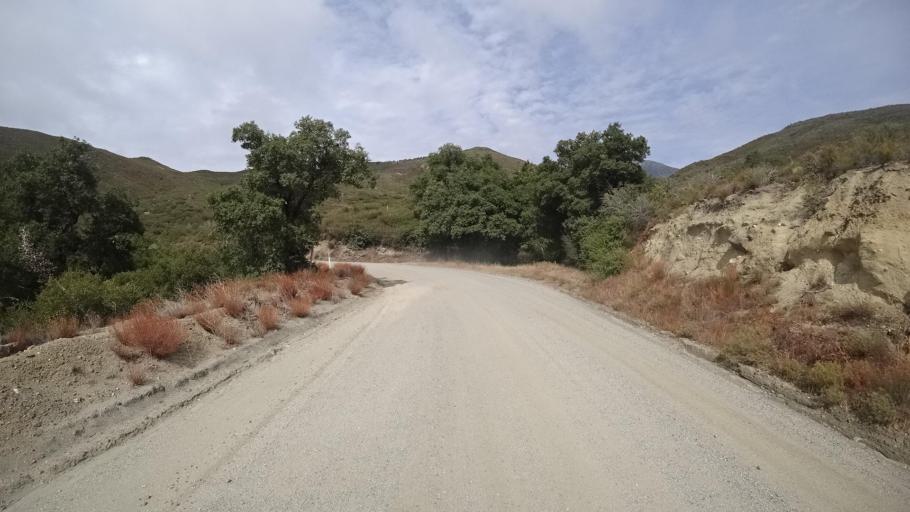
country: US
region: California
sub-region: San Diego County
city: Descanso
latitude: 32.9256
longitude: -116.6308
